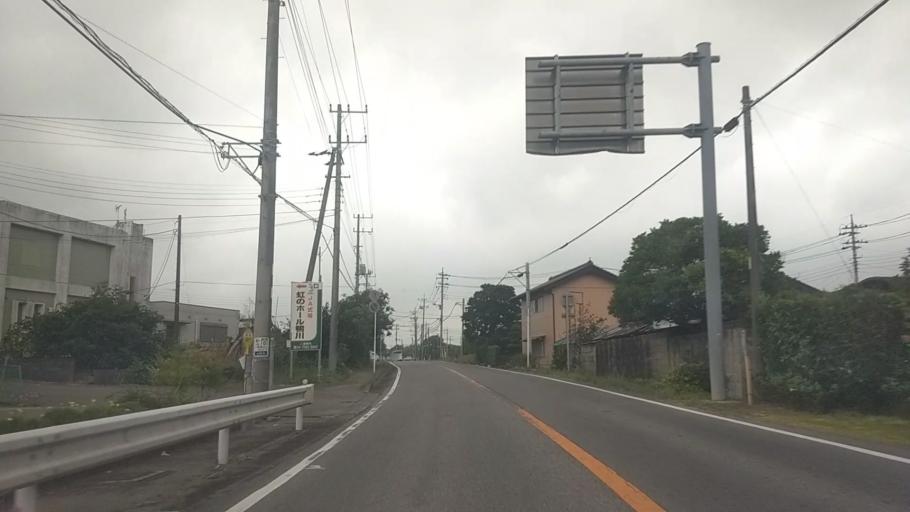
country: JP
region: Chiba
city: Kawaguchi
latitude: 35.1217
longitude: 140.0685
